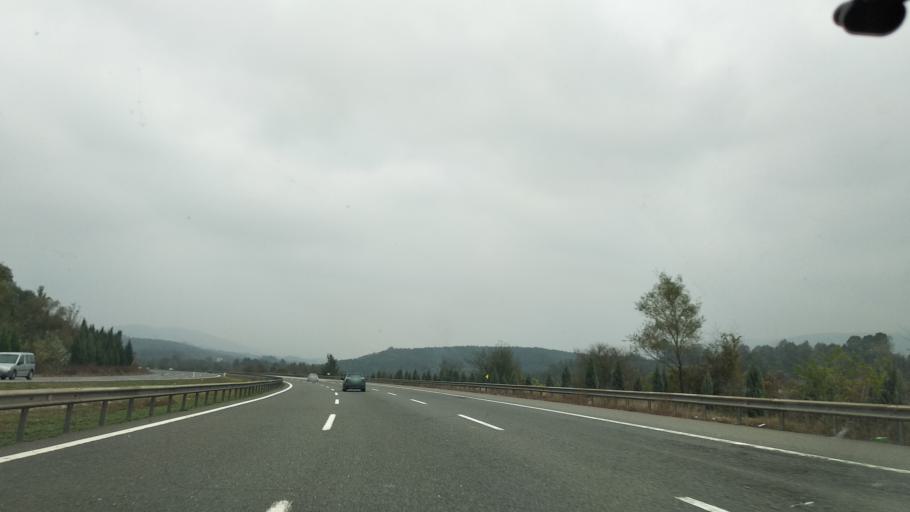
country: TR
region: Sakarya
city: Hendek
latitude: 40.7710
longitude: 30.7804
